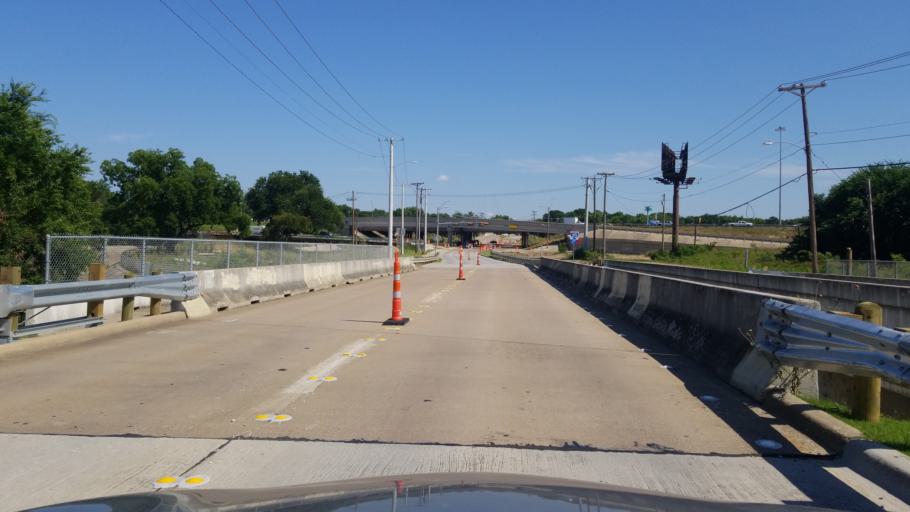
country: US
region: Texas
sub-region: Dallas County
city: Grand Prairie
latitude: 32.6780
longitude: -97.0174
